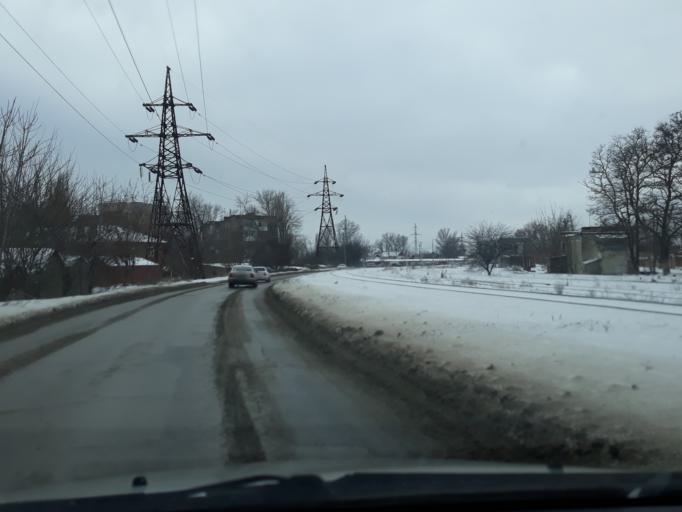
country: RU
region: Rostov
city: Taganrog
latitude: 47.2466
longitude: 38.8834
